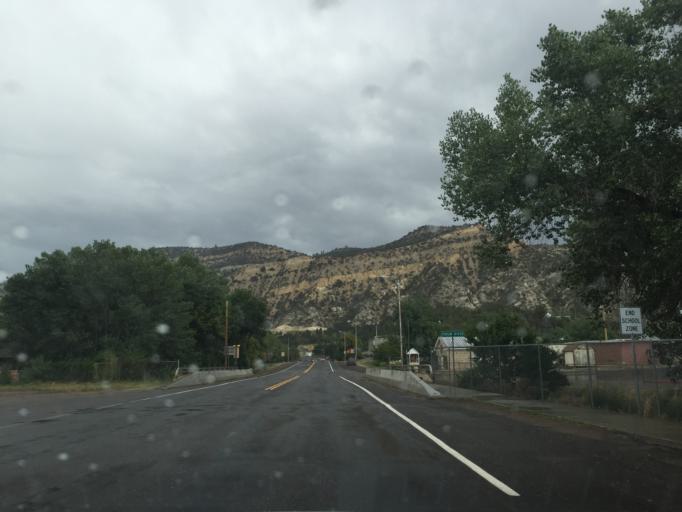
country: US
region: Utah
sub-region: Kane County
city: Kanab
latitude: 37.2760
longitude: -112.6370
